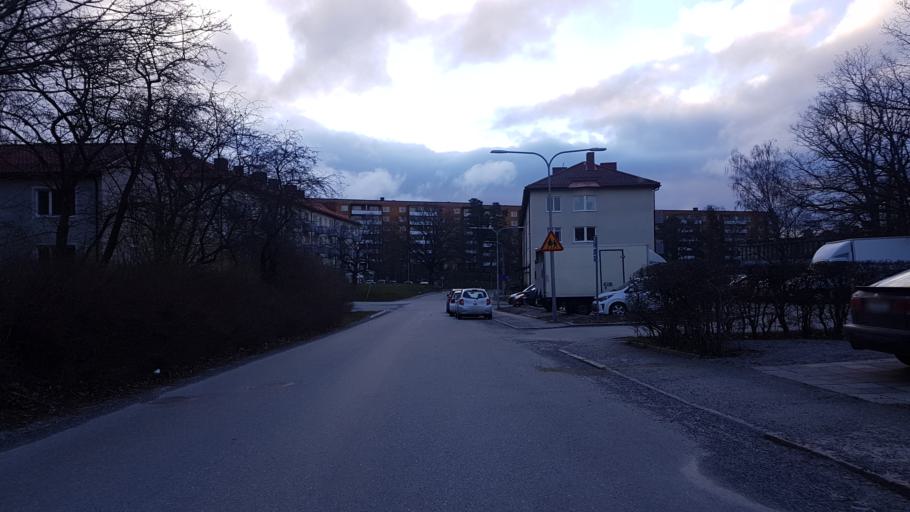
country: SE
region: Stockholm
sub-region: Lidingo
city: Lidingoe
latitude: 59.3533
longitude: 18.1465
